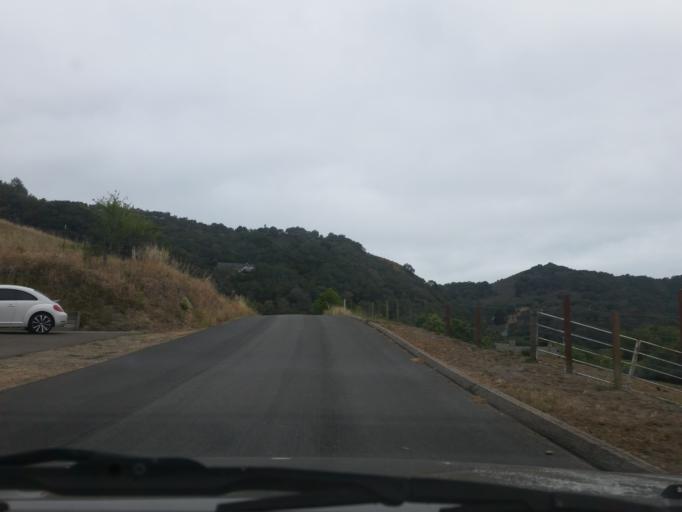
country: US
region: California
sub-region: San Luis Obispo County
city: Avila Beach
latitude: 35.1877
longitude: -120.6965
